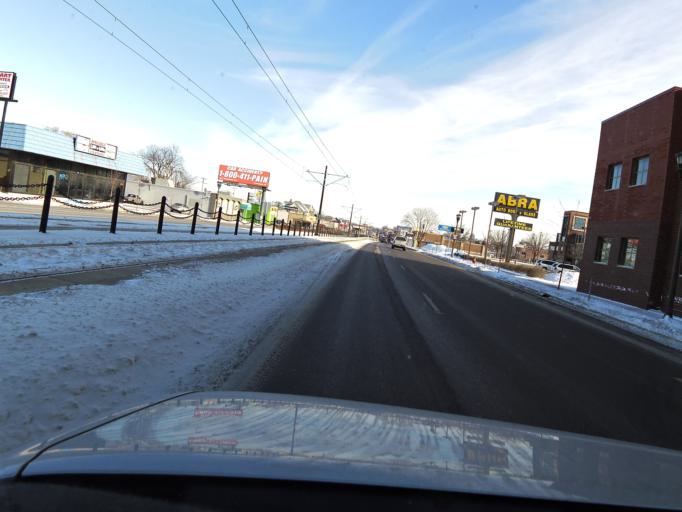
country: US
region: Minnesota
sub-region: Ramsey County
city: Falcon Heights
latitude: 44.9556
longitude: -93.1512
